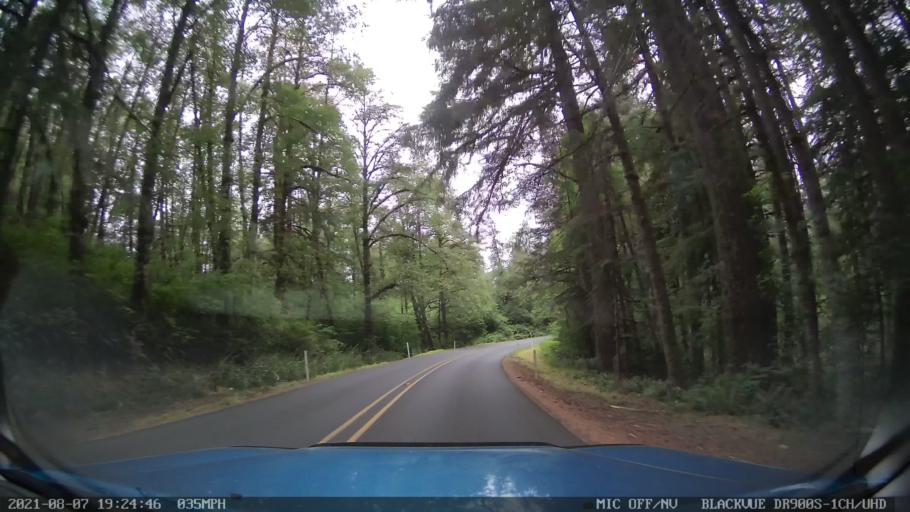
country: US
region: Oregon
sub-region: Linn County
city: Lyons
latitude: 44.8559
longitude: -122.6575
